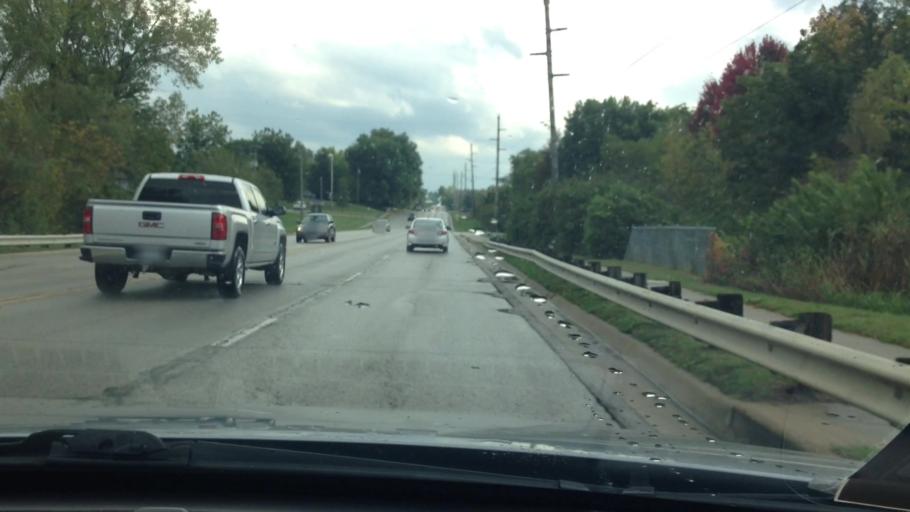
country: US
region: Kansas
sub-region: Leavenworth County
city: Leavenworth
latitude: 39.2809
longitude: -94.9279
